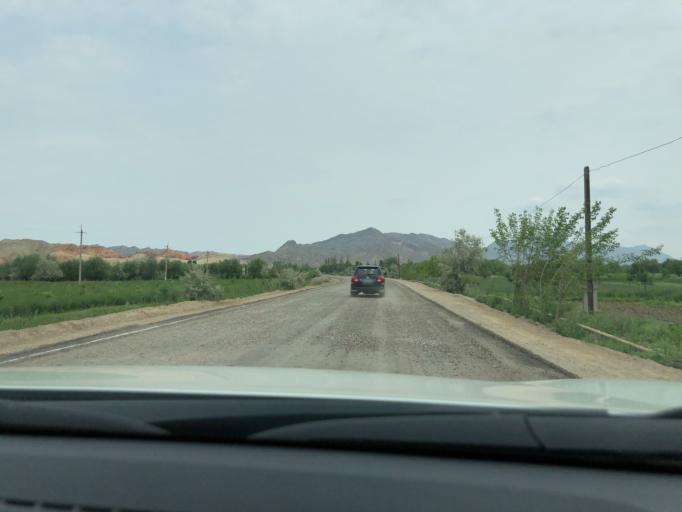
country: TJ
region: Viloyati Sughd
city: Isfara
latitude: 40.1532
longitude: 70.6257
